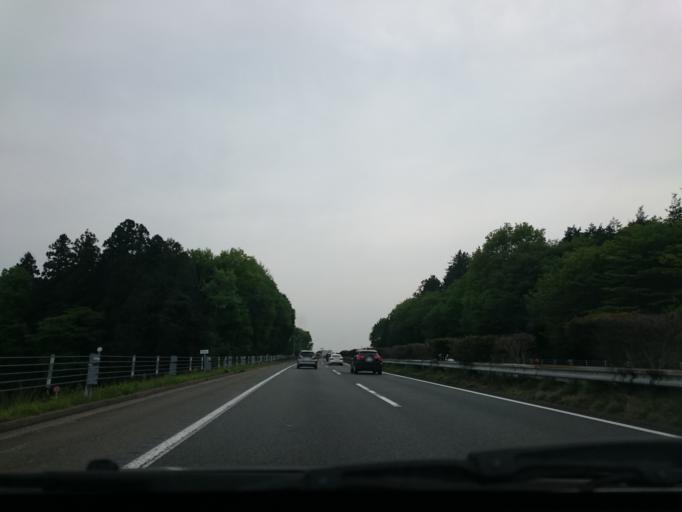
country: JP
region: Tochigi
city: Utsunomiya-shi
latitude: 36.6438
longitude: 139.8541
